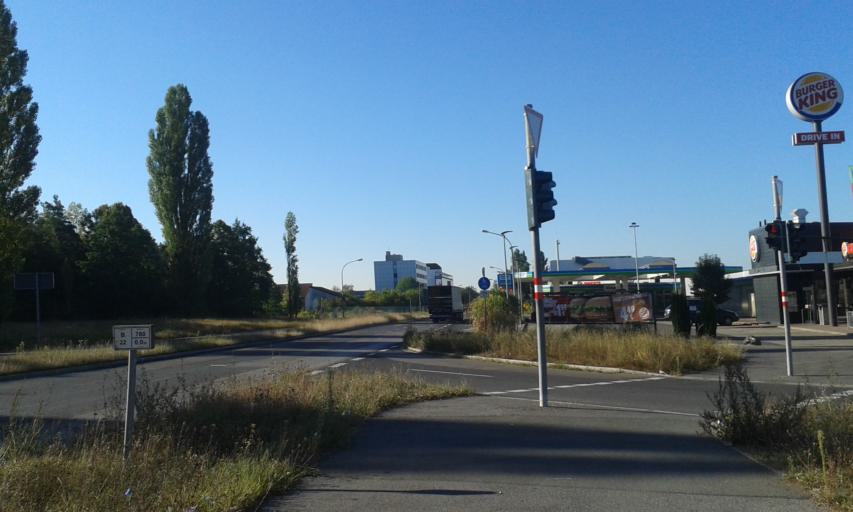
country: DE
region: Bavaria
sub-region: Upper Franconia
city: Bamberg
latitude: 49.8879
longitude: 10.9222
